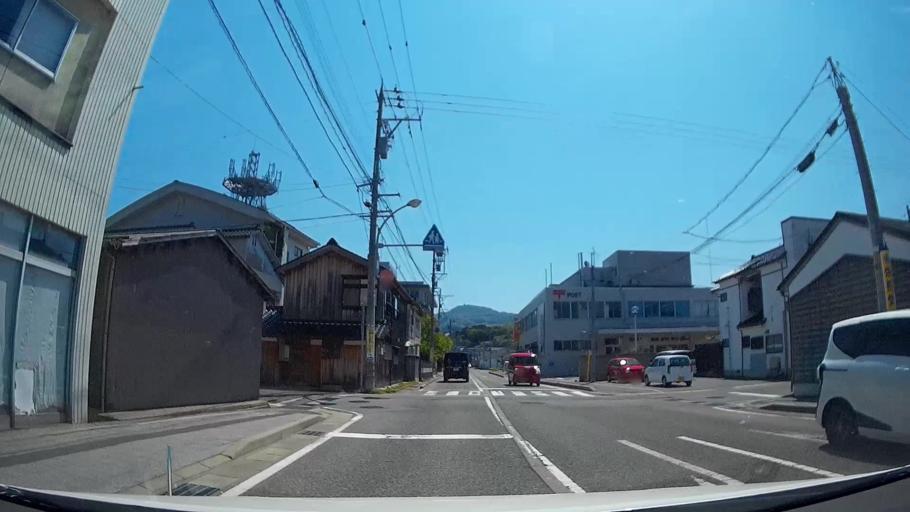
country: JP
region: Ishikawa
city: Nanao
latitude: 37.3936
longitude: 136.9051
